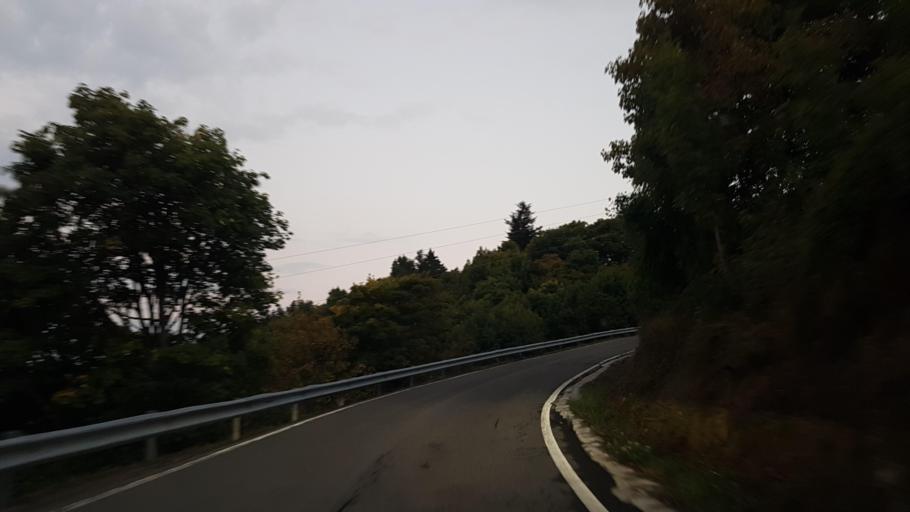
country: IT
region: Liguria
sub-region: Provincia di La Spezia
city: Varese Ligure
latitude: 44.4273
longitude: 9.6219
